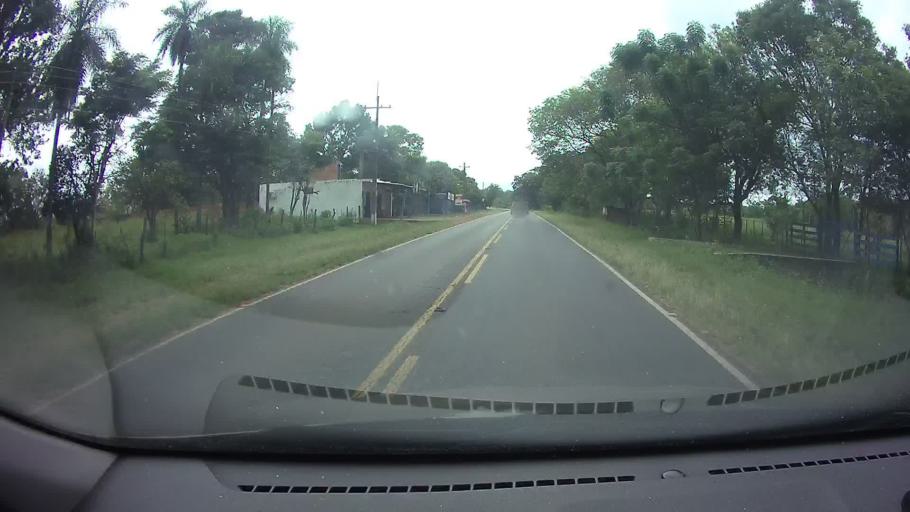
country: PY
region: Central
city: Nueva Italia
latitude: -25.5706
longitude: -57.5039
